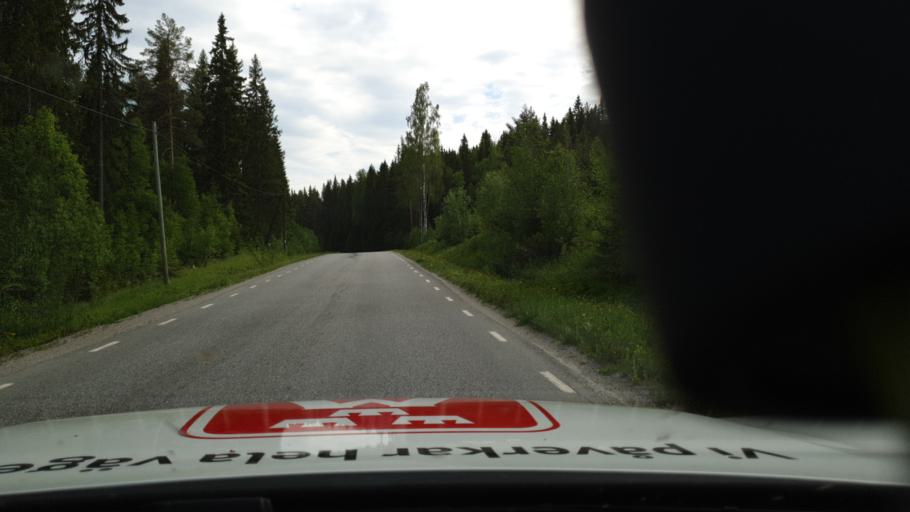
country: SE
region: Jaemtland
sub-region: Braecke Kommun
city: Braecke
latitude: 62.9960
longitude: 15.1972
